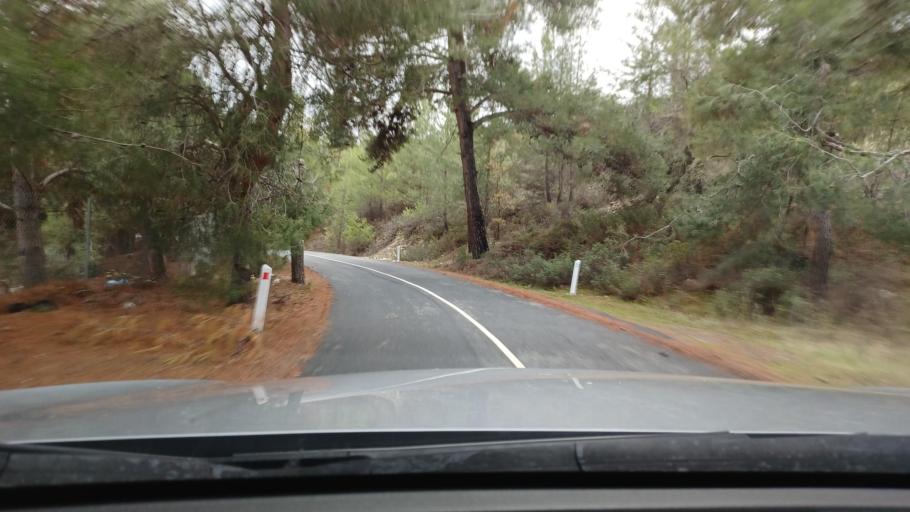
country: CY
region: Limassol
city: Pelendri
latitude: 34.8545
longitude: 32.8845
